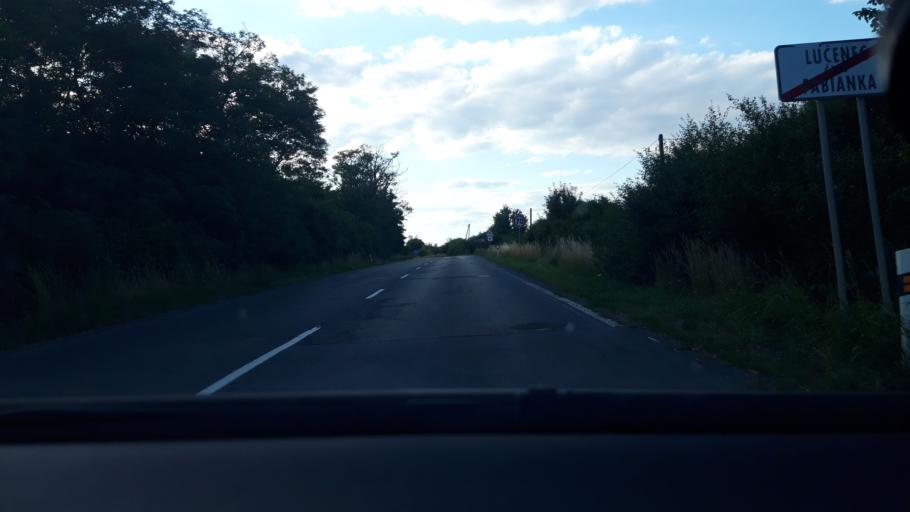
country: SK
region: Banskobystricky
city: Lucenec
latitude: 48.3247
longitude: 19.6976
